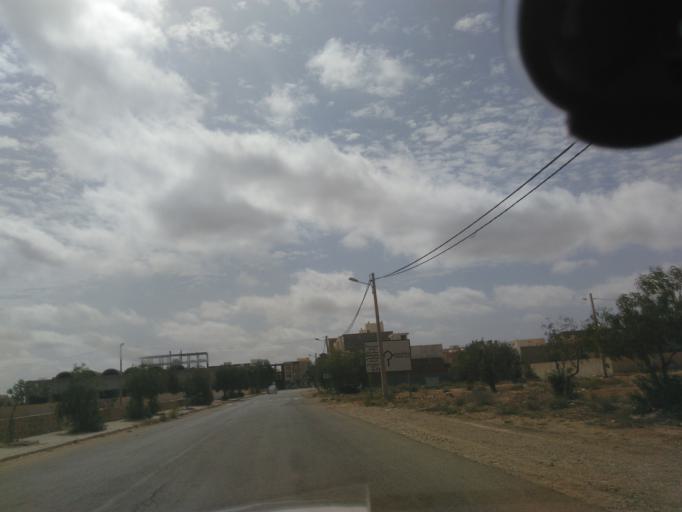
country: TN
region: Tataouine
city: Tataouine
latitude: 32.9556
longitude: 10.4668
